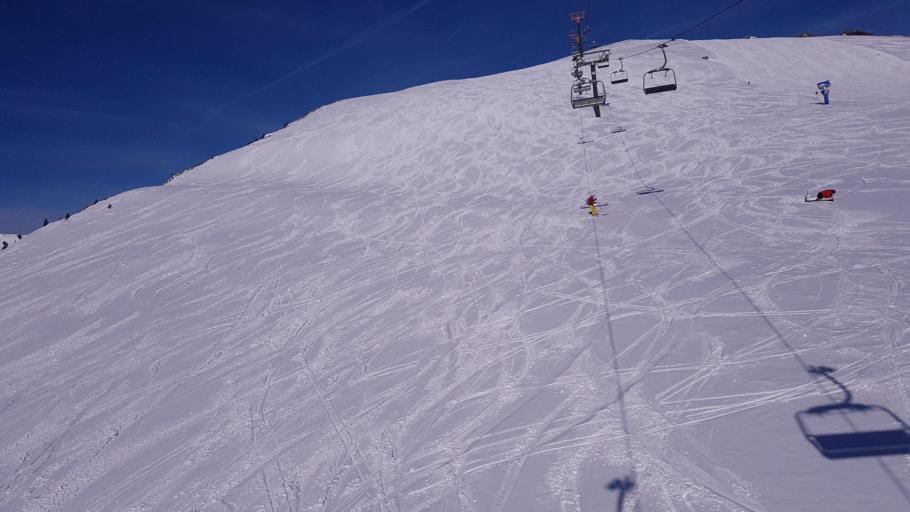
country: AT
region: Salzburg
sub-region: Politischer Bezirk Zell am See
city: Neukirchen am Grossvenediger
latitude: 47.2815
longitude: 12.2657
